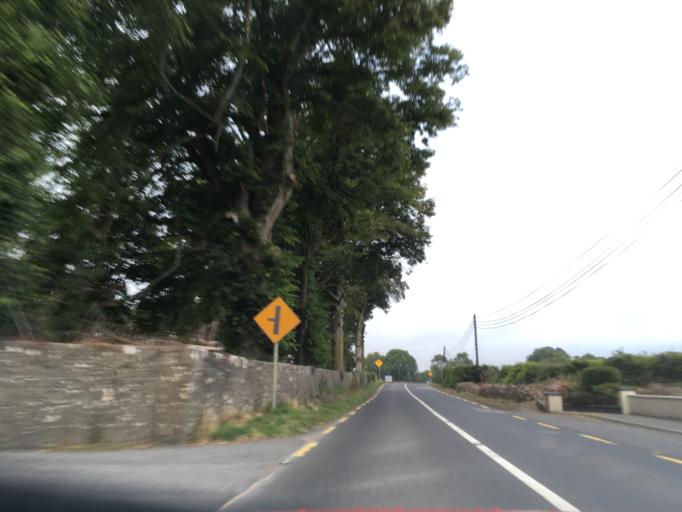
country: IE
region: Munster
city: Cashel
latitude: 52.4964
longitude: -7.9962
